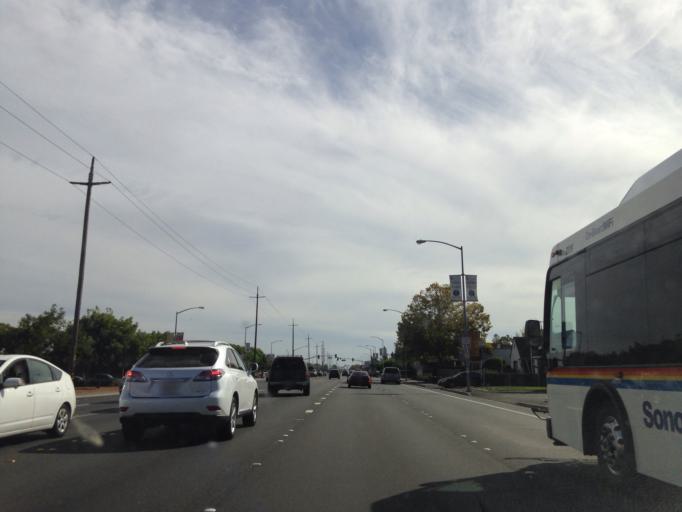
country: US
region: California
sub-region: Sonoma County
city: Roseland
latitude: 38.4209
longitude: -122.7136
